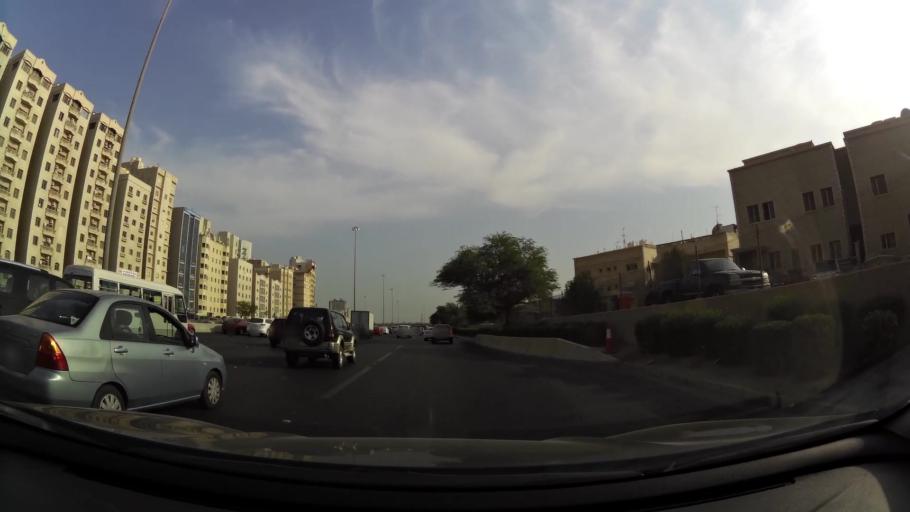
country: KW
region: Muhafazat Hawalli
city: Hawalli
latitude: 29.3272
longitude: 48.0090
